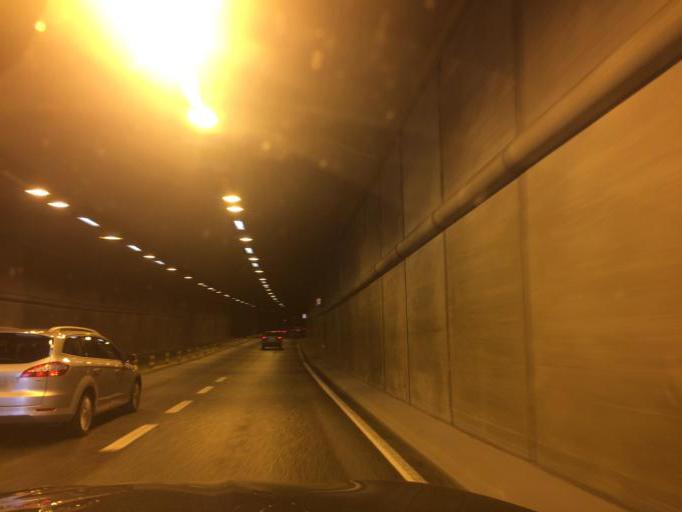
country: NO
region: Vest-Agder
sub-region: Kristiansand
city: Kristiansand
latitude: 58.1556
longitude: 8.0021
